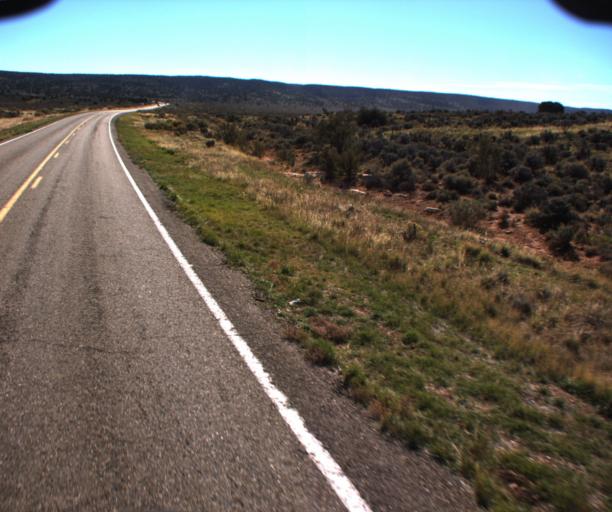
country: US
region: Arizona
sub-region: Coconino County
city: Fredonia
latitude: 36.8514
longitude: -112.2902
